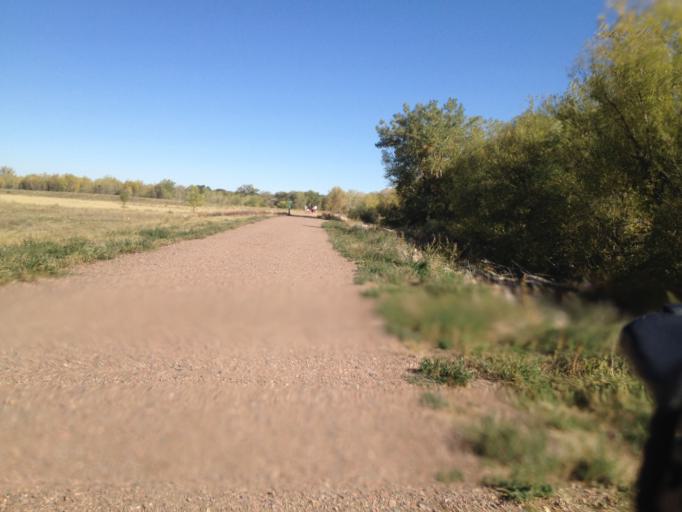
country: US
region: Colorado
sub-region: Boulder County
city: Boulder
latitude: 39.9717
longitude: -105.2318
